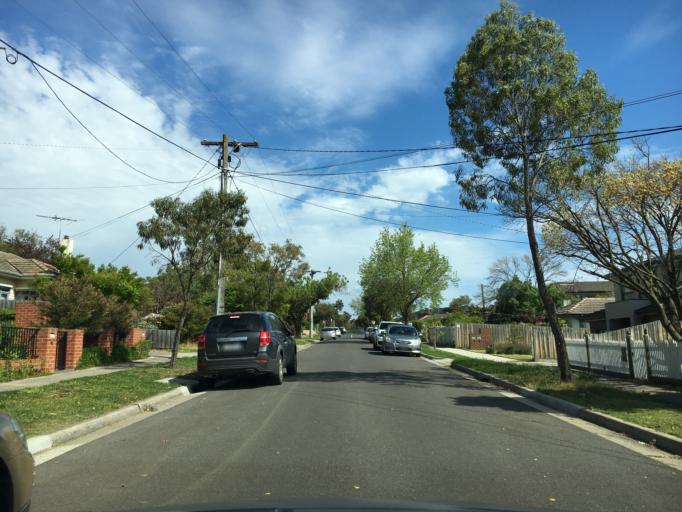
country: AU
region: Victoria
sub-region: Monash
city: Chadstone
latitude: -37.8937
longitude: 145.1136
